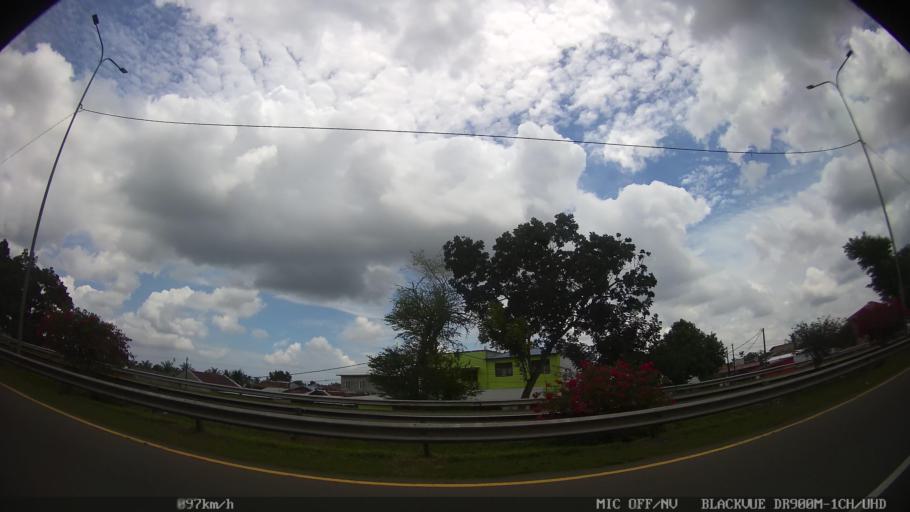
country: ID
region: North Sumatra
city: Medan
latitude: 3.6290
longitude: 98.7183
